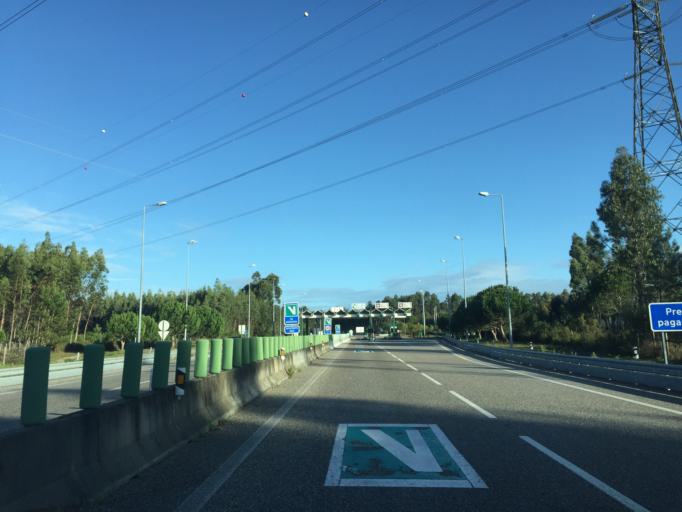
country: PT
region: Coimbra
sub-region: Figueira da Foz
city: Lavos
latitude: 40.0462
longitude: -8.8145
